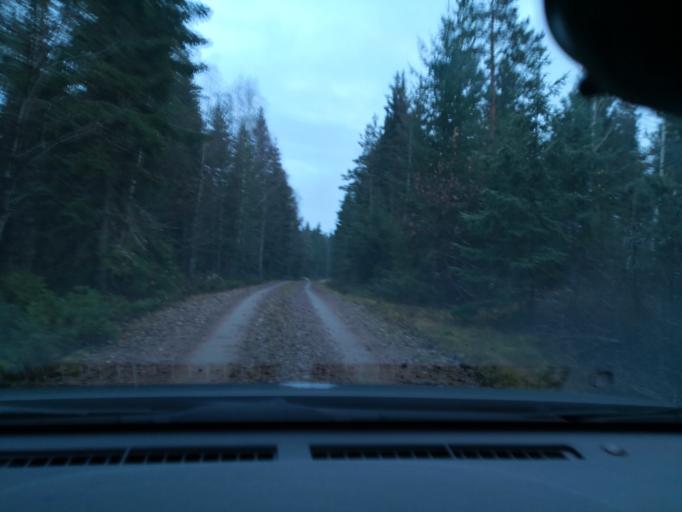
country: SE
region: Vaestmanland
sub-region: Hallstahammars Kommun
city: Kolback
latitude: 59.5534
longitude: 16.1645
